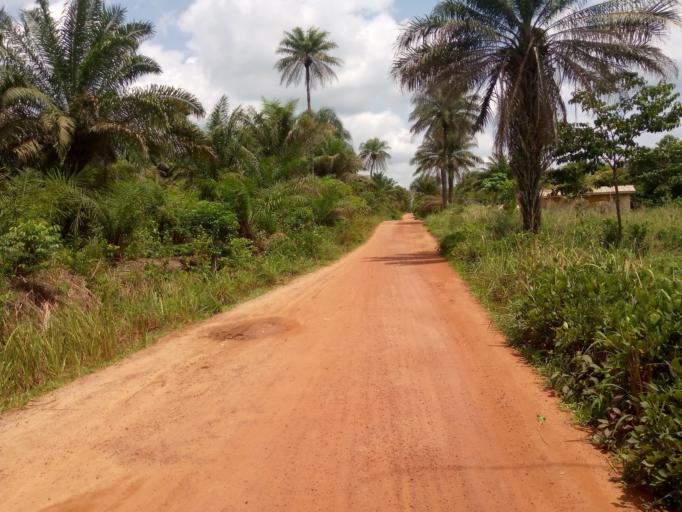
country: SL
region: Western Area
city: Waterloo
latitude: 8.3800
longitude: -12.9695
